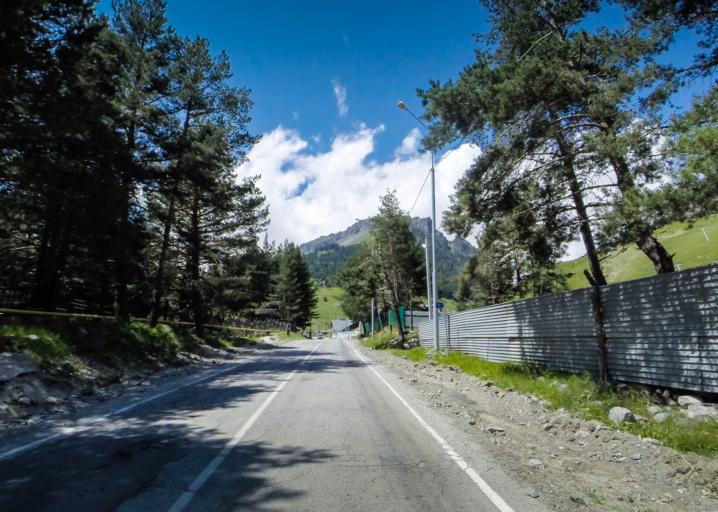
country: RU
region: Kabardino-Balkariya
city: Terskol
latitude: 43.2545
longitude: 42.5181
